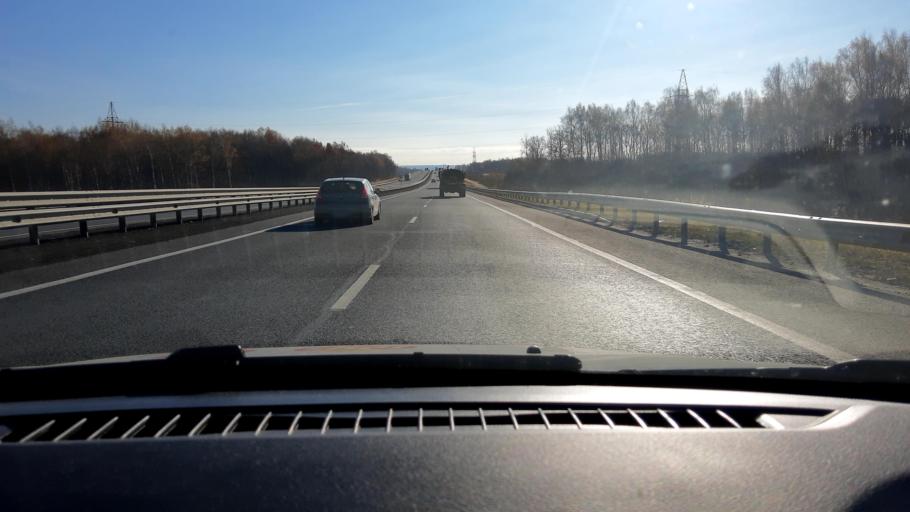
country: RU
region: Nizjnij Novgorod
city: Burevestnik
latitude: 56.1413
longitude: 43.7602
